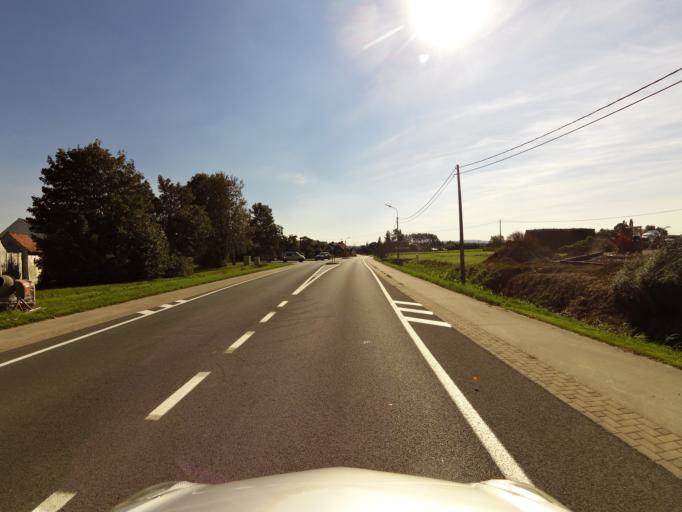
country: BE
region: Flanders
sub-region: Provincie West-Vlaanderen
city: Poperinge
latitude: 50.8713
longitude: 2.7356
